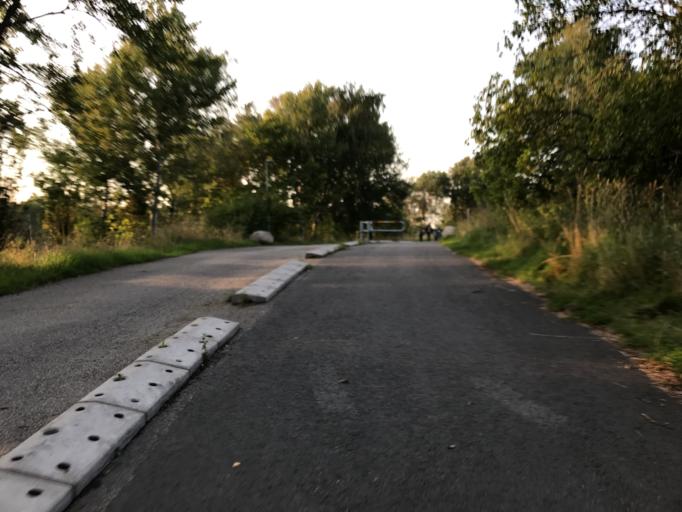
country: SE
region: Vaestra Goetaland
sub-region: Goteborg
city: Majorna
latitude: 57.7289
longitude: 11.8867
